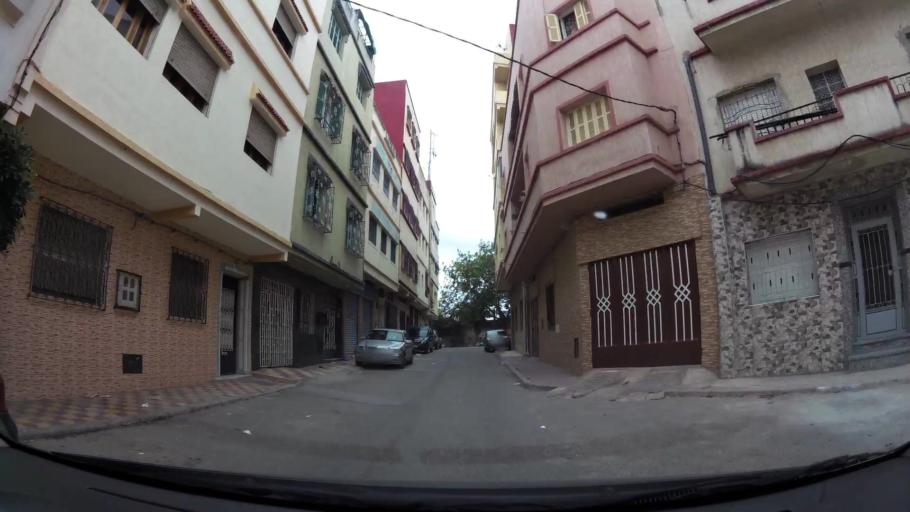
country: MA
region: Tanger-Tetouan
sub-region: Tanger-Assilah
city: Tangier
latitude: 35.7722
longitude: -5.8182
